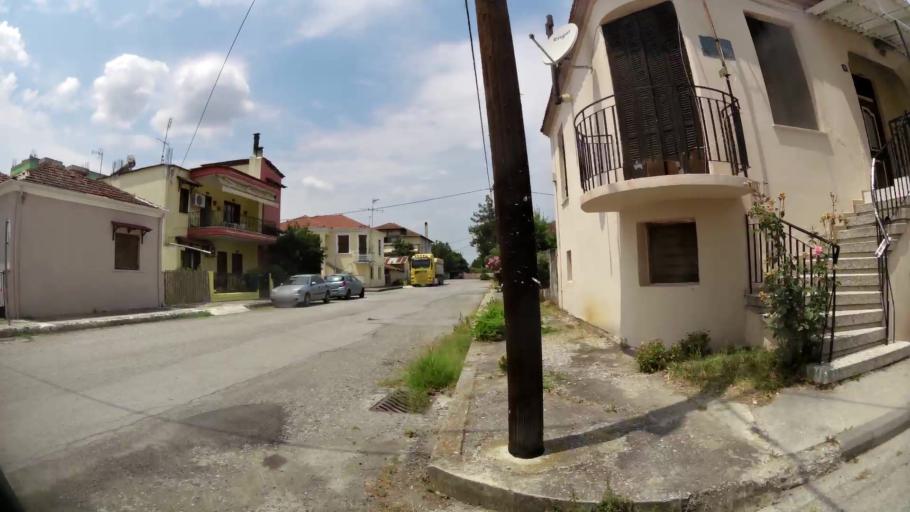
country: GR
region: Central Macedonia
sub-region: Nomos Pierias
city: Peristasi
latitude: 40.2751
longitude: 22.5388
